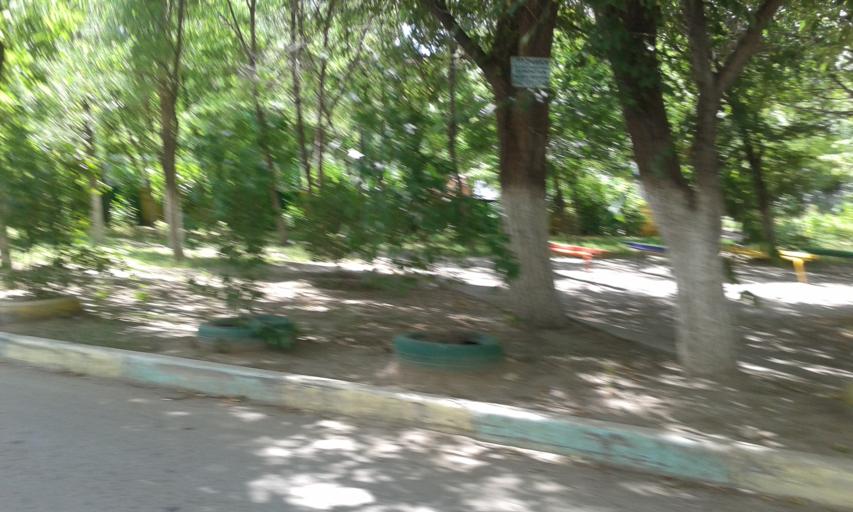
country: RU
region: Volgograd
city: Volgograd
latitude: 48.7545
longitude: 44.5111
